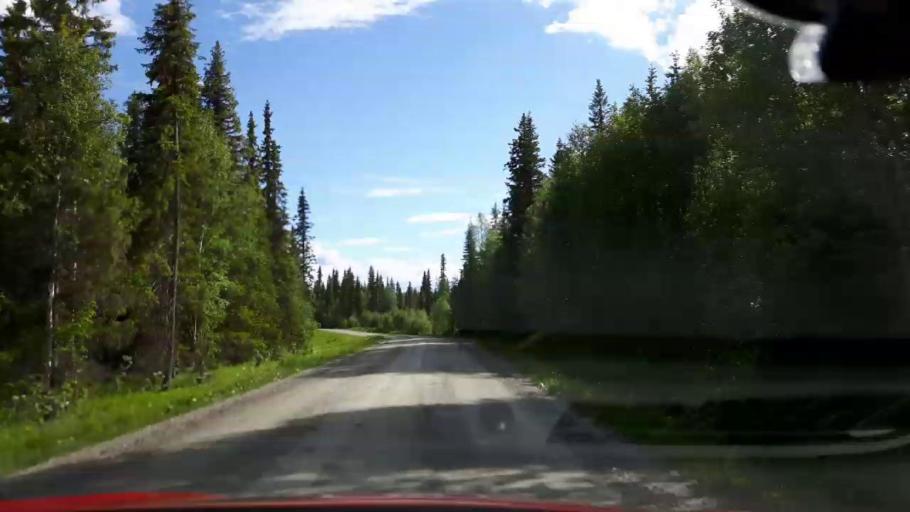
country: SE
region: Jaemtland
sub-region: Krokoms Kommun
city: Valla
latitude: 63.8067
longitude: 14.0497
